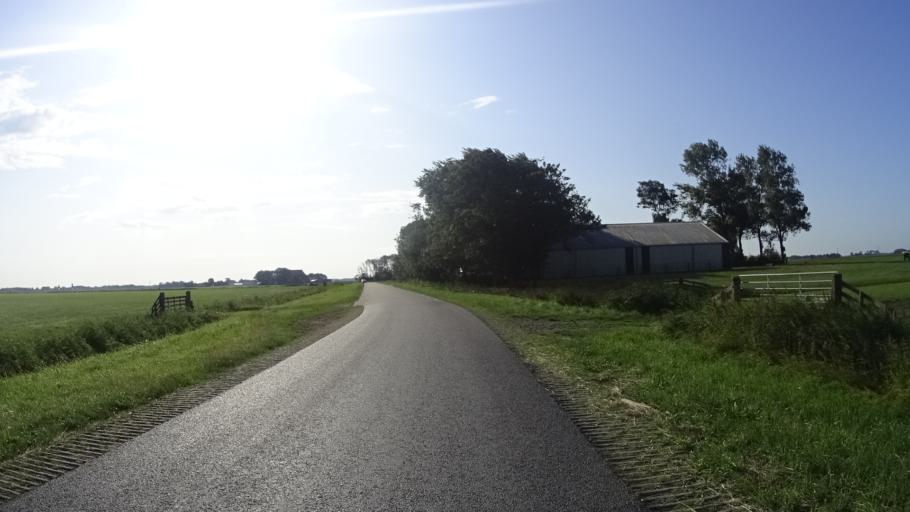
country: NL
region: Friesland
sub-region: Sudwest Fryslan
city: Makkum
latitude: 53.1137
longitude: 5.4051
